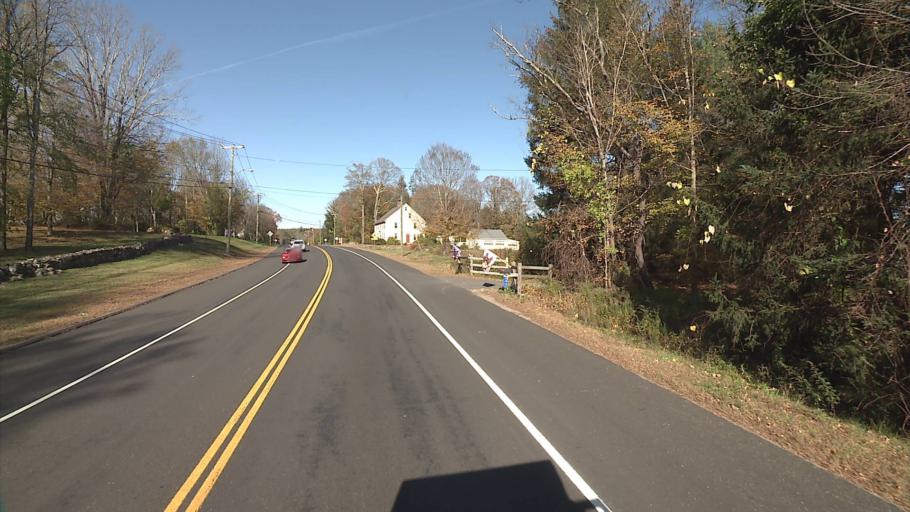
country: US
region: Connecticut
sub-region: Tolland County
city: Coventry Lake
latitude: 41.7460
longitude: -72.3869
